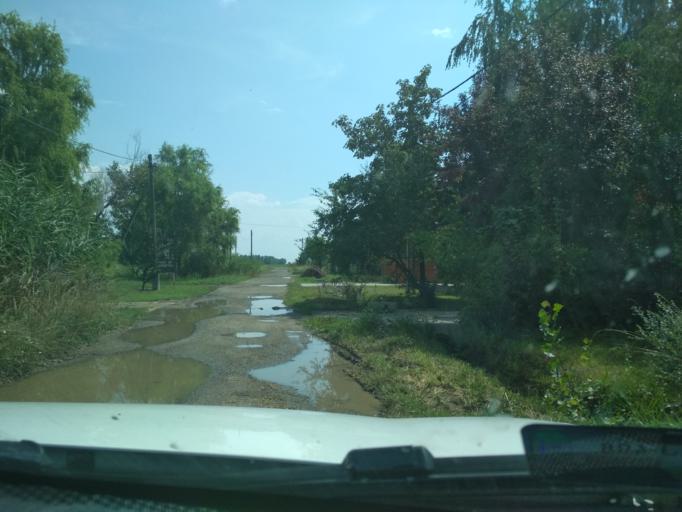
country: HU
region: Jasz-Nagykun-Szolnok
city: Abadszalok
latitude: 47.4701
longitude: 20.5840
